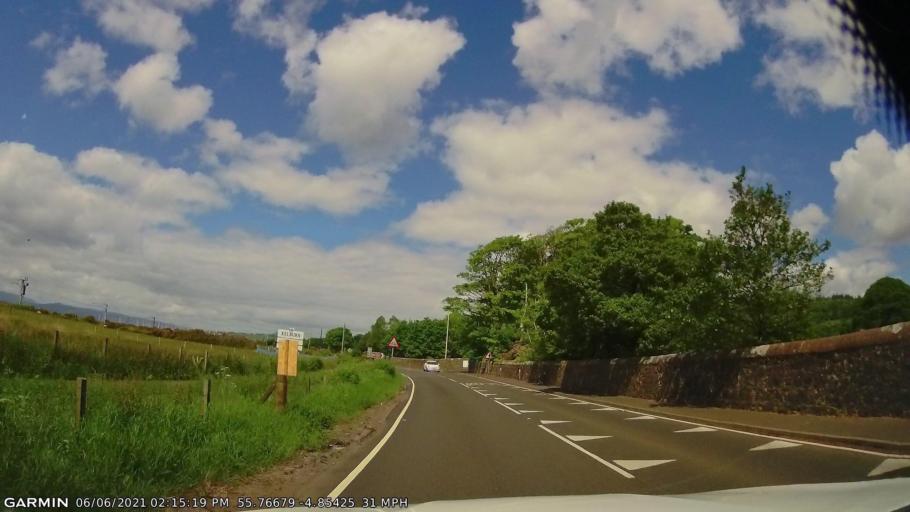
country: GB
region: Scotland
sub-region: North Ayrshire
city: Fairlie
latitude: 55.7668
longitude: -4.8544
